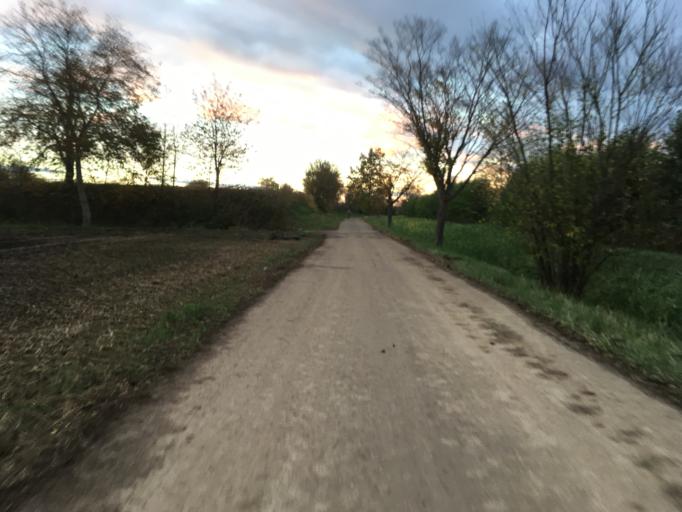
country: DE
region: Baden-Wuerttemberg
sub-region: Freiburg Region
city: Eichstetten
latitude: 48.1077
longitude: 7.7462
